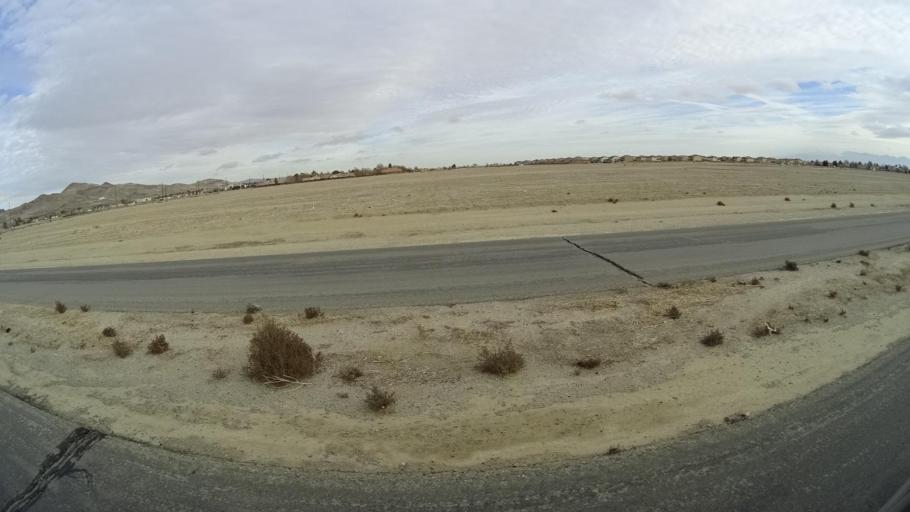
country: US
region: California
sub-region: Kern County
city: Rosamond
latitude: 34.8606
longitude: -118.2033
